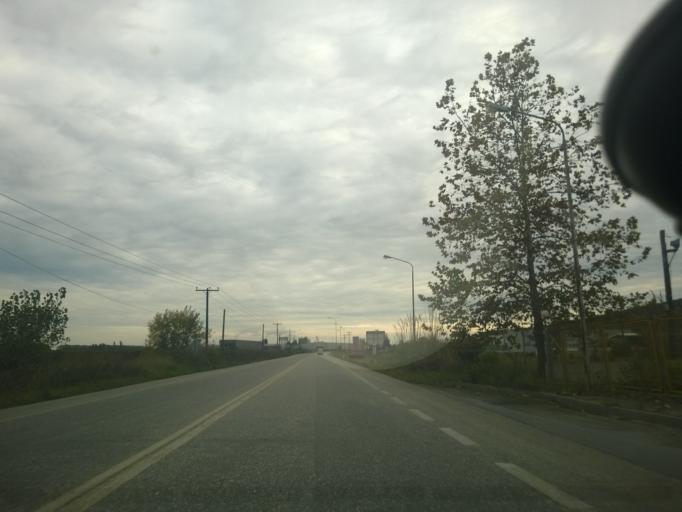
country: GR
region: Central Macedonia
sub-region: Nomos Pellis
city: Profitis Ilias
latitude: 40.8001
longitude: 22.1523
